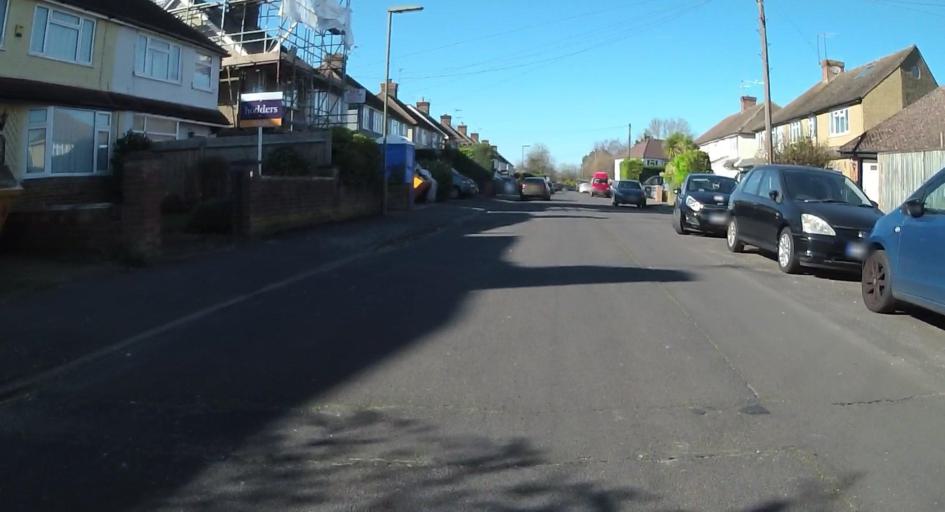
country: GB
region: England
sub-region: Surrey
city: Addlestone
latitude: 51.3701
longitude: -0.4785
